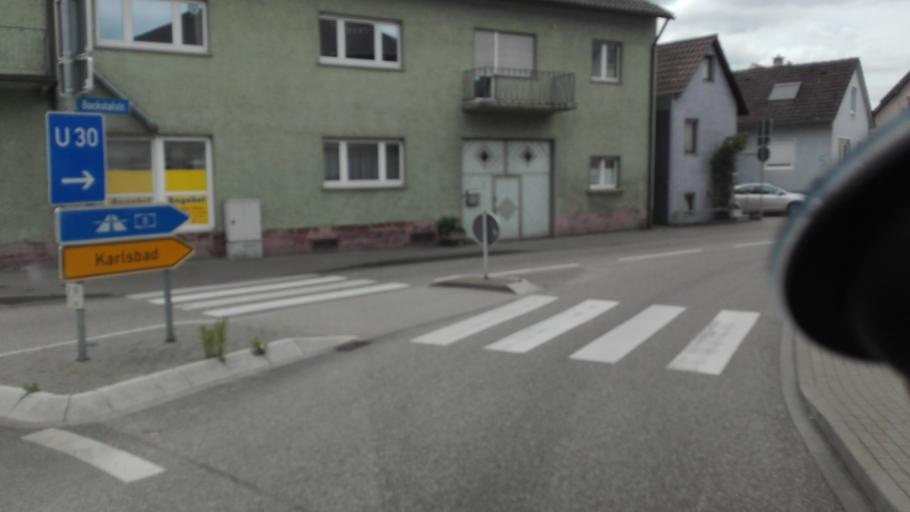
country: DE
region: Baden-Wuerttemberg
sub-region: Karlsruhe Region
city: Konigsbach-Stein
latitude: 48.9667
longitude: 8.5537
